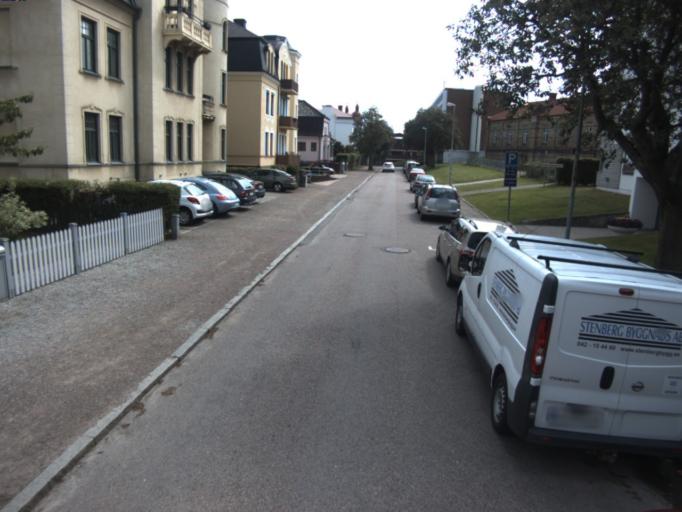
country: SE
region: Skane
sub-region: Helsingborg
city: Helsingborg
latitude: 56.0497
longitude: 12.7032
